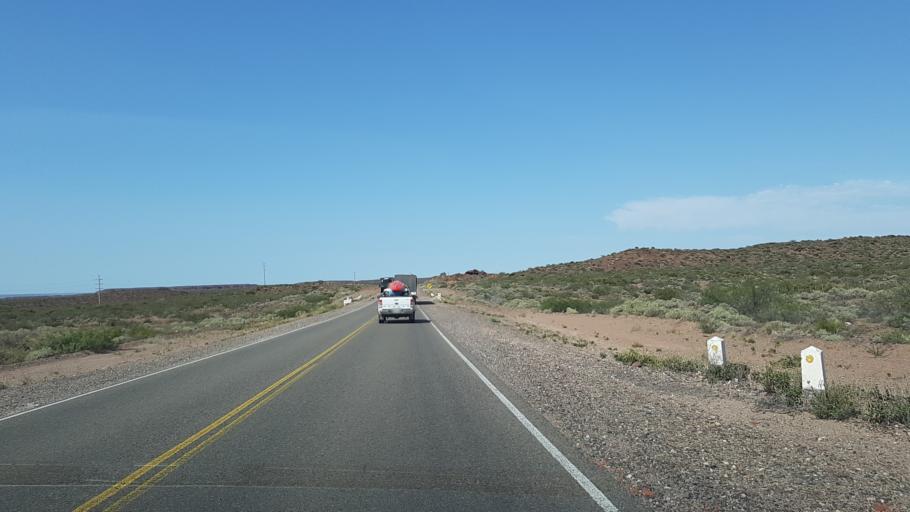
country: AR
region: Neuquen
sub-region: Departamento de Picun Leufu
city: Picun Leufu
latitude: -39.2811
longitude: -68.8612
